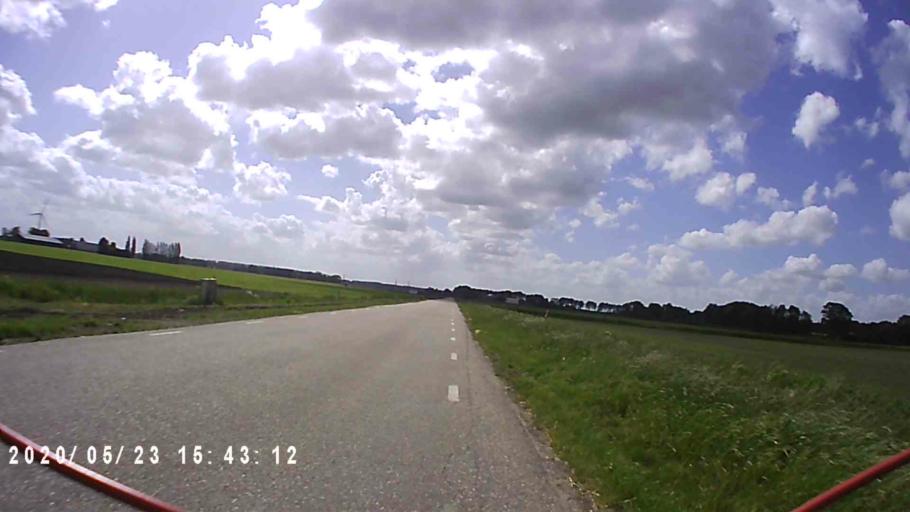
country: NL
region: Groningen
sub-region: Gemeente Delfzijl
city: Delfzijl
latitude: 53.2804
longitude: 6.9231
